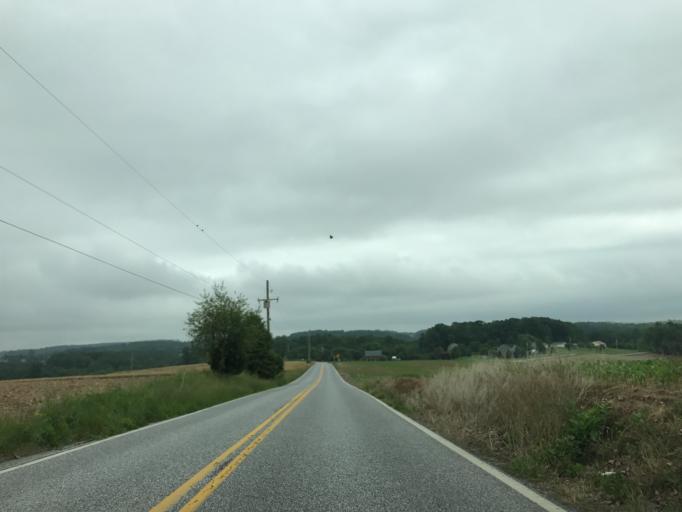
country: US
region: Pennsylvania
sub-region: York County
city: Susquehanna Trails
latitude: 39.7553
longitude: -76.4605
